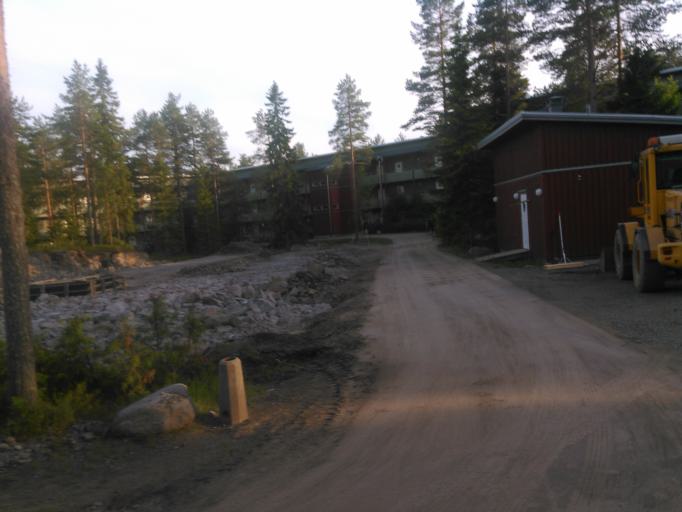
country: SE
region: Vaesterbotten
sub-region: Umea Kommun
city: Umea
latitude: 63.8158
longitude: 20.3110
